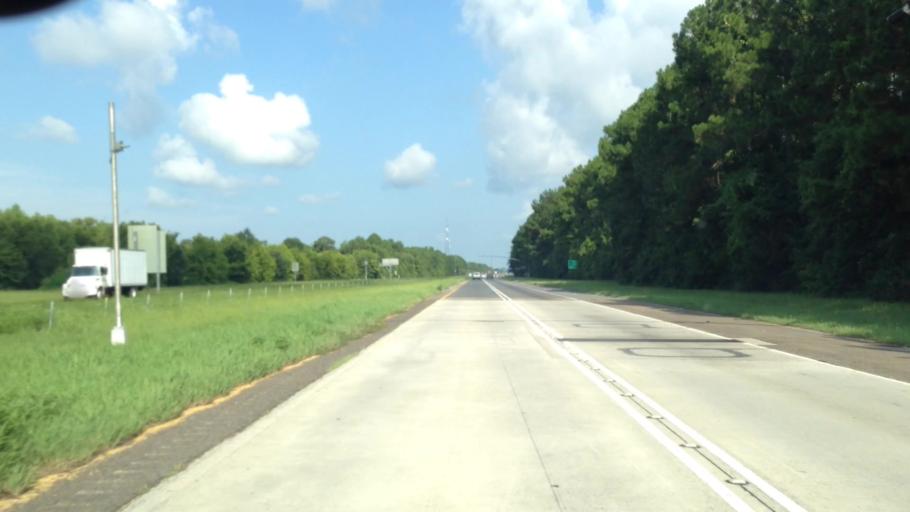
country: US
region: Louisiana
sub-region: Saint John the Baptist Parish
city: Laplace
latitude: 30.0960
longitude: -90.4677
